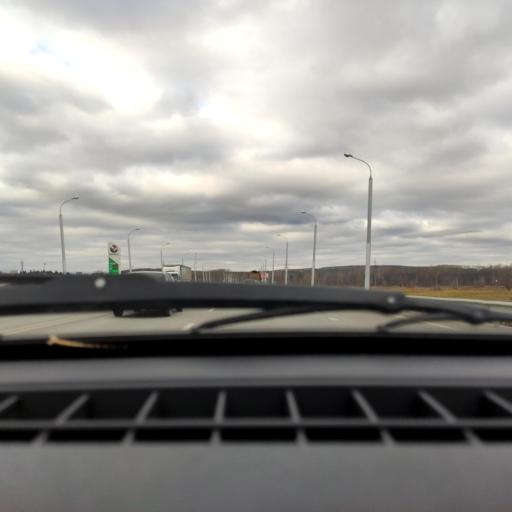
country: RU
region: Bashkortostan
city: Ufa
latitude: 54.8058
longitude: 56.1793
